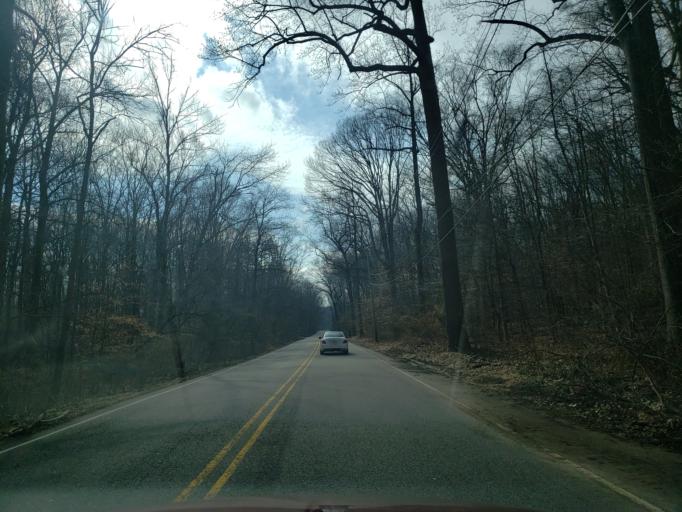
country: US
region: New Jersey
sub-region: Essex County
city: Short Hills
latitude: 40.7473
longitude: -74.3005
